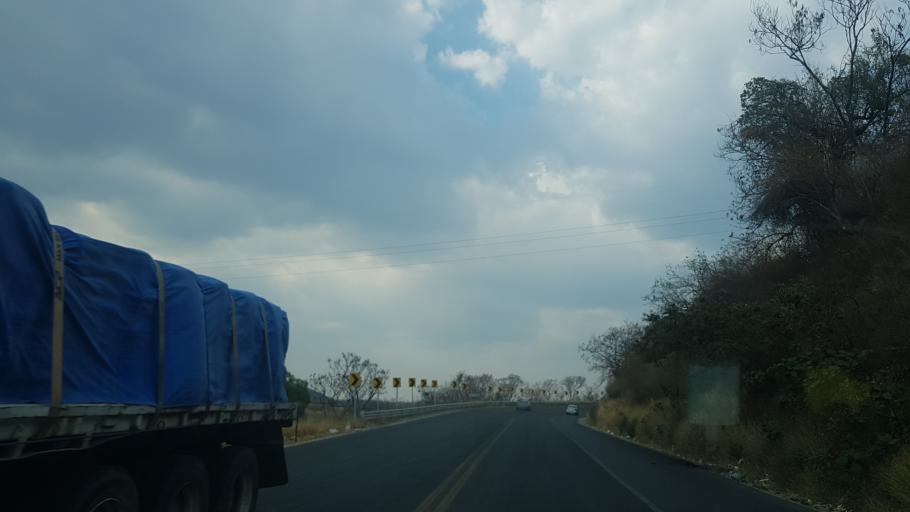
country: MX
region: Puebla
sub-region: Santa Isabel Cholula
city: Santa Ana Acozautla
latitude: 18.9515
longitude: -98.3893
